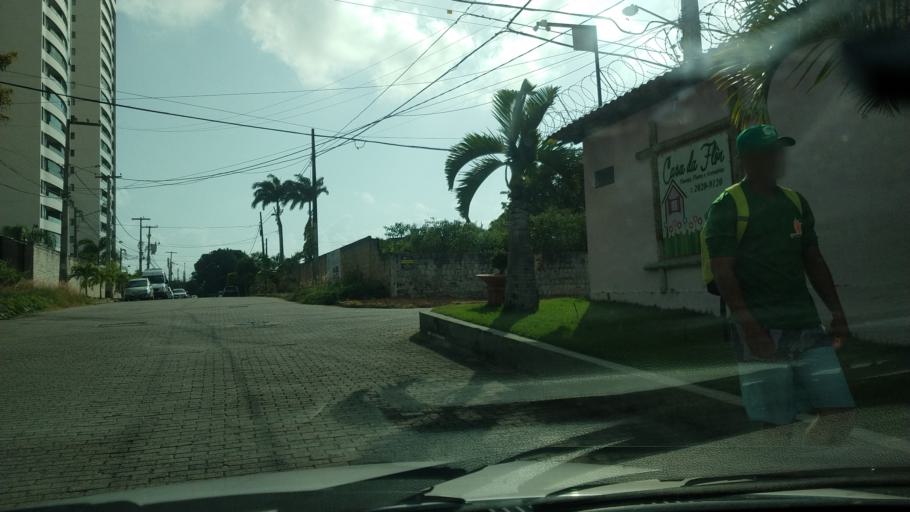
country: BR
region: Rio Grande do Norte
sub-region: Natal
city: Natal
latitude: -5.8567
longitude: -35.2011
